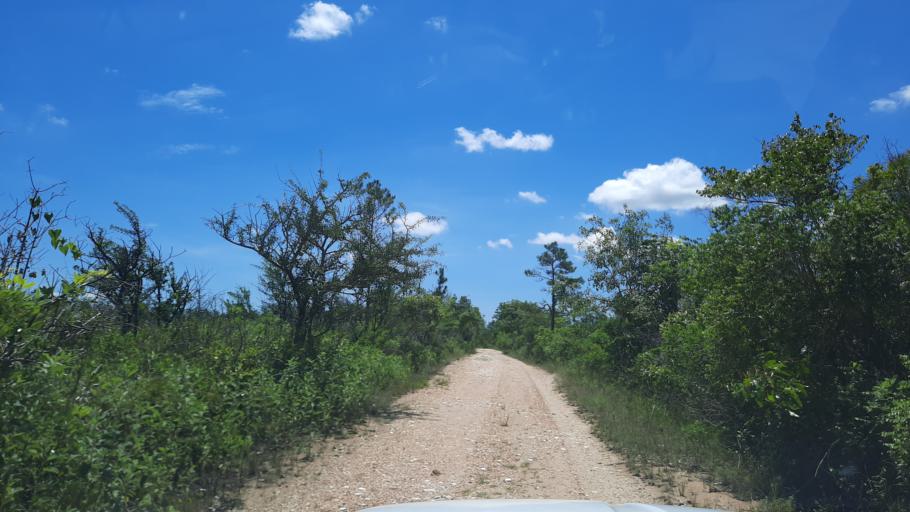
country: BZ
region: Cayo
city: Belmopan
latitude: 17.3553
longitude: -88.5462
